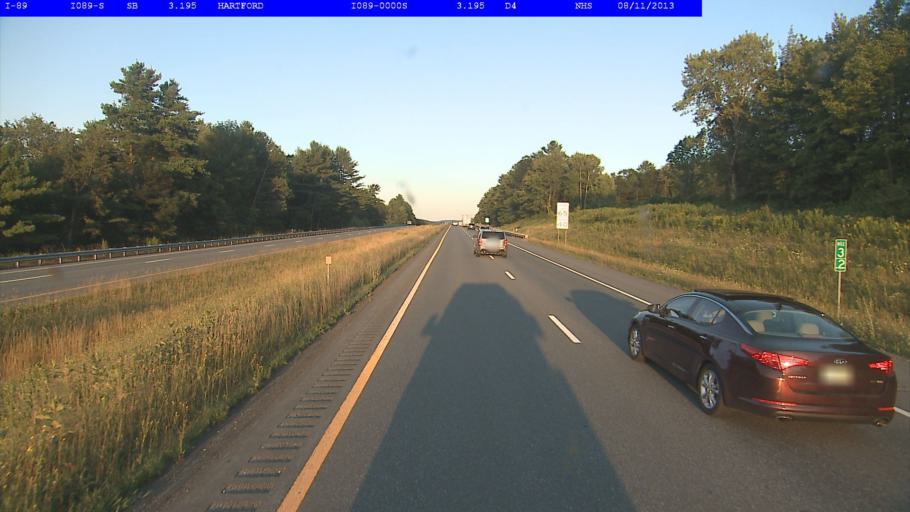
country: US
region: Vermont
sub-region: Windsor County
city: White River Junction
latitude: 43.6624
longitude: -72.3731
